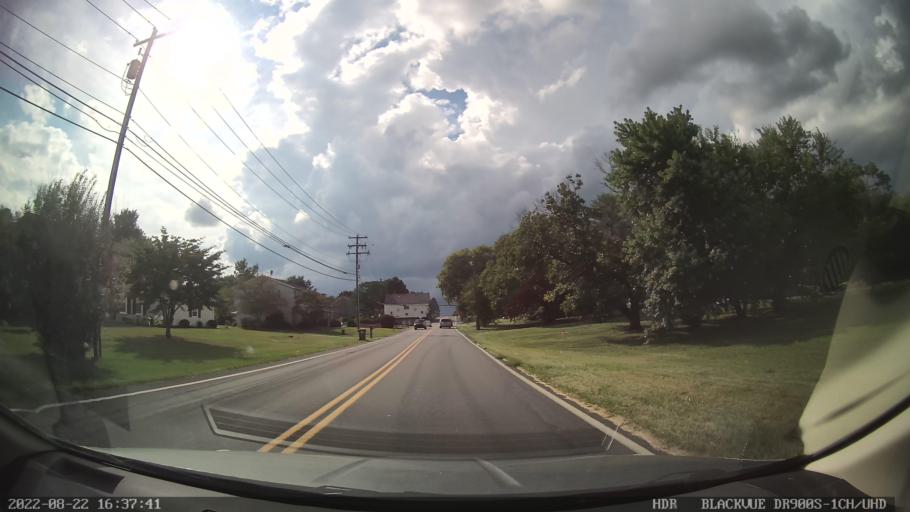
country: US
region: Pennsylvania
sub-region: Lehigh County
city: Wescosville
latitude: 40.5654
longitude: -75.5363
